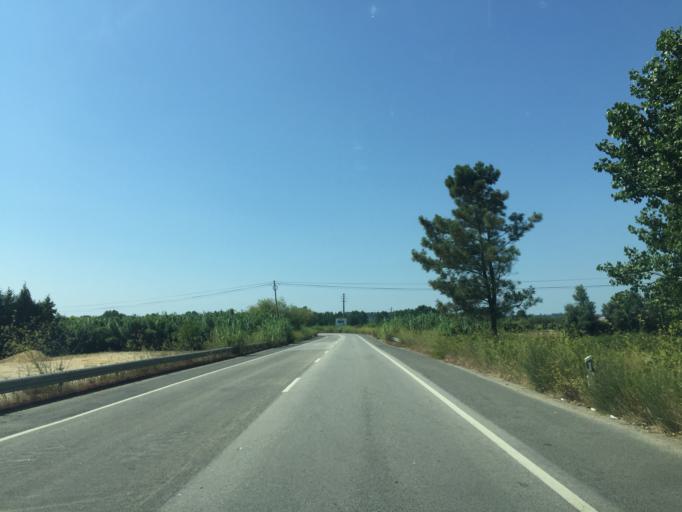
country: PT
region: Aveiro
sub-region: Mealhada
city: Mealhada
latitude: 40.3718
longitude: -8.4700
